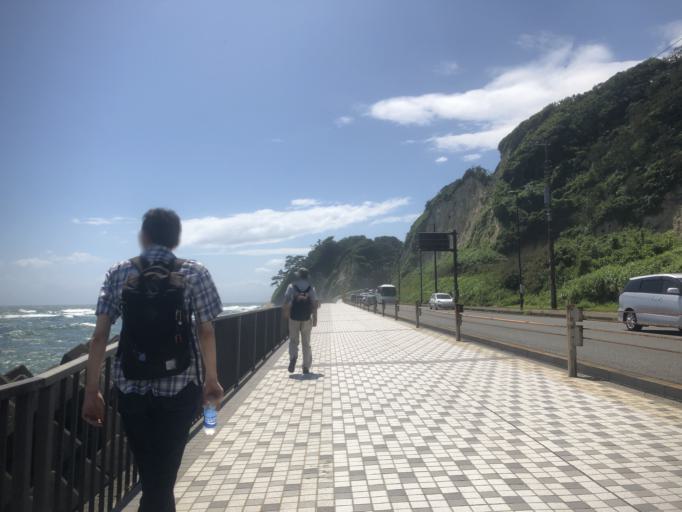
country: JP
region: Kanagawa
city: Kamakura
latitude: 35.3037
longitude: 139.5314
